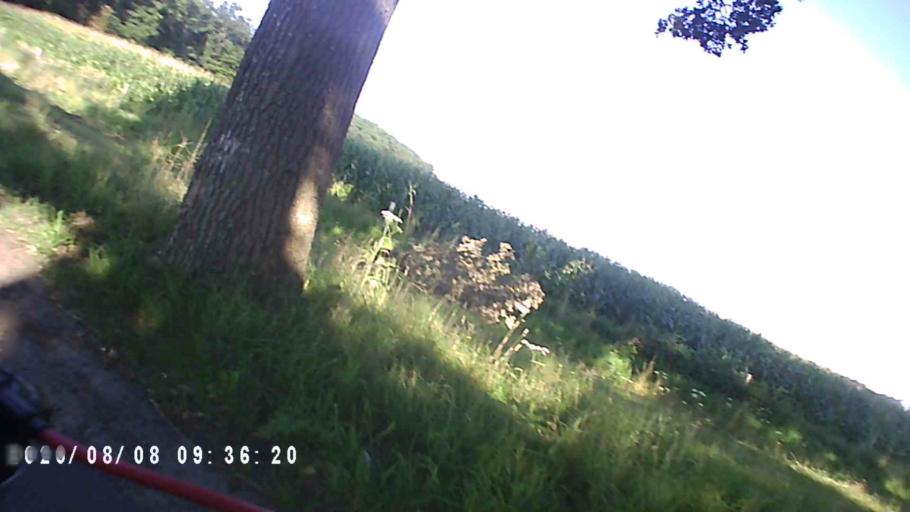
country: NL
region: Groningen
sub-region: Gemeente Leek
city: Leek
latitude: 53.0496
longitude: 6.3850
